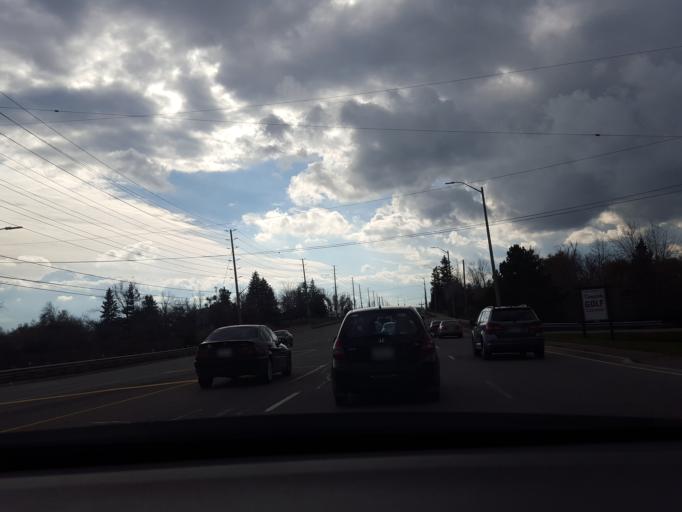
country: CA
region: Ontario
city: Brampton
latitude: 43.6427
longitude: -79.7101
